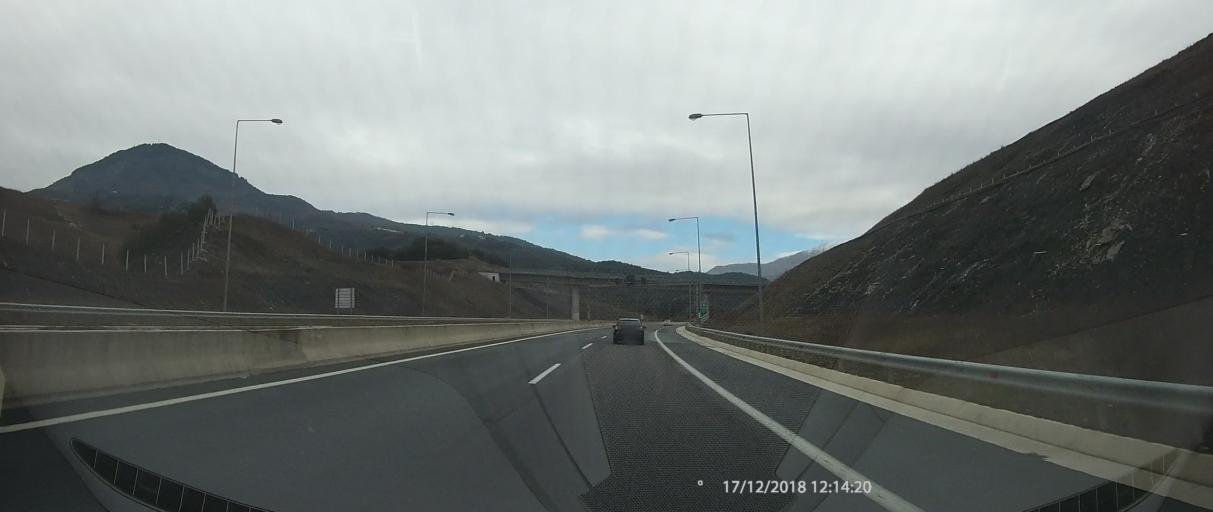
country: GR
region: Epirus
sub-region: Nomos Ioanninon
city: Katsikas
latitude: 39.7176
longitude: 20.9946
